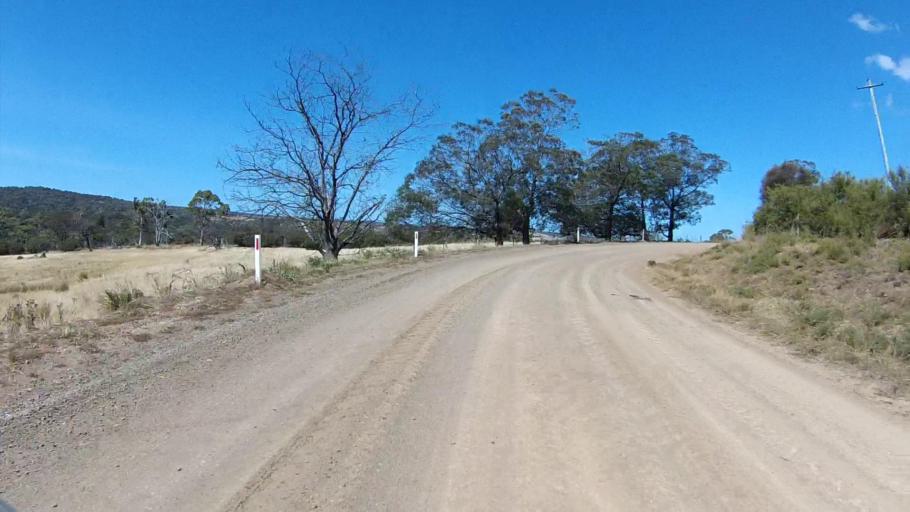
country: AU
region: Tasmania
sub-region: Break O'Day
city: St Helens
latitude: -41.9727
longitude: 148.0728
